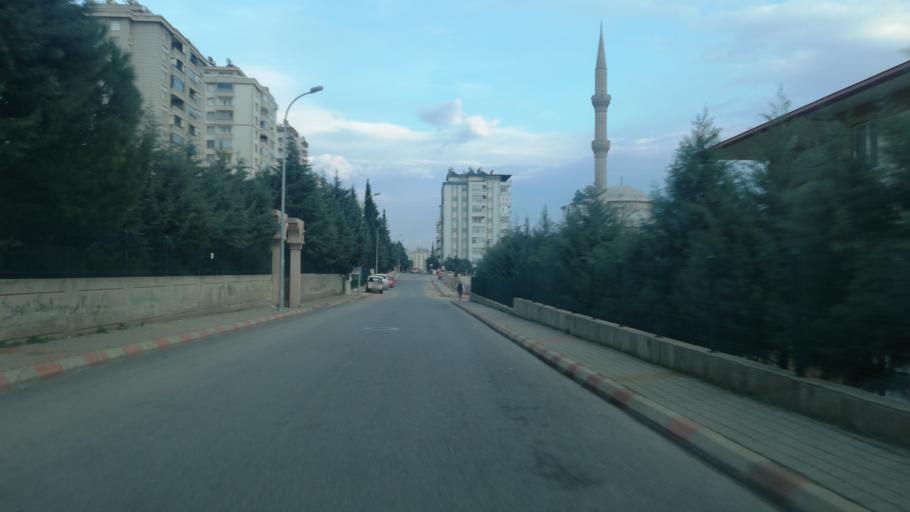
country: TR
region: Kahramanmaras
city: Kahramanmaras
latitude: 37.5872
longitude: 36.8897
